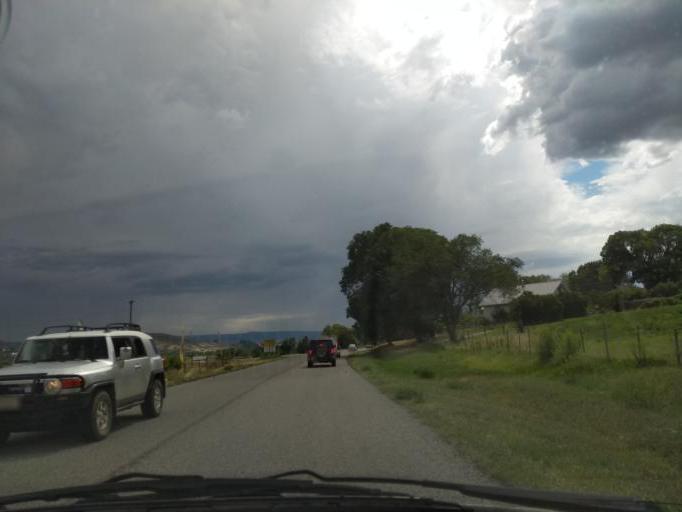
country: US
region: Colorado
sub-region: Delta County
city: Paonia
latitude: 38.8866
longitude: -107.5869
